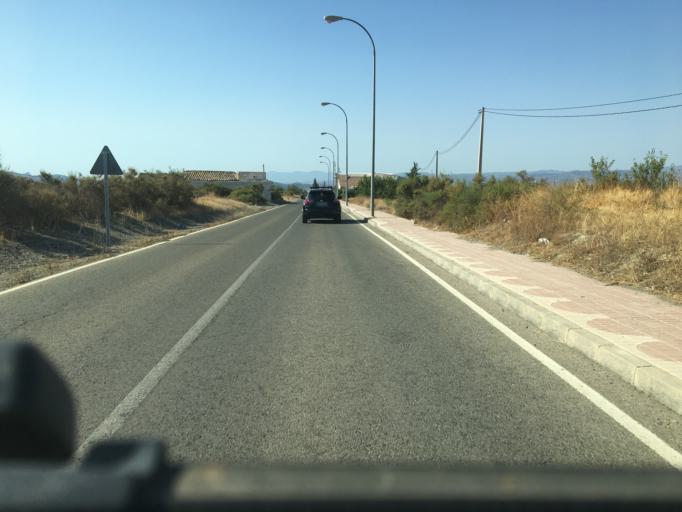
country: ES
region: Andalusia
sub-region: Provincia de Almeria
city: Huercal-Overa
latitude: 37.4569
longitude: -1.9890
